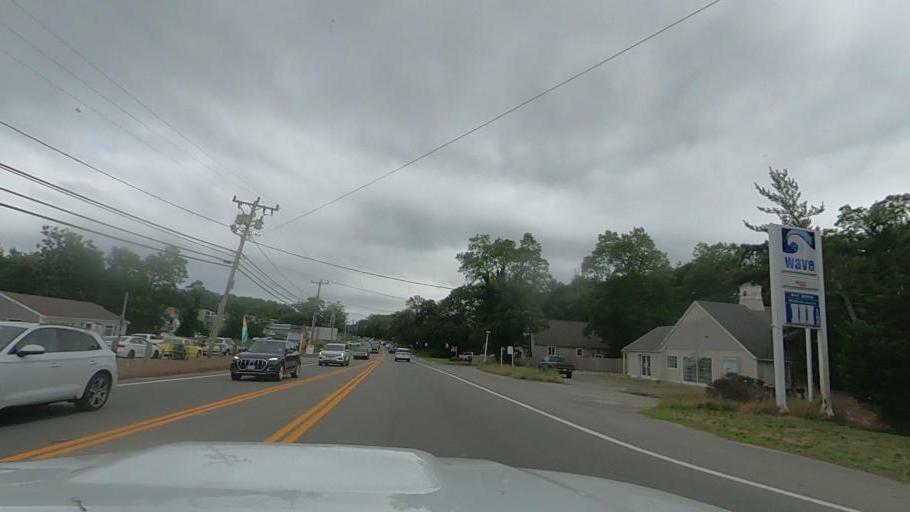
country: US
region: Massachusetts
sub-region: Barnstable County
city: Wellfleet
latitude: 41.9353
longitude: -70.0207
